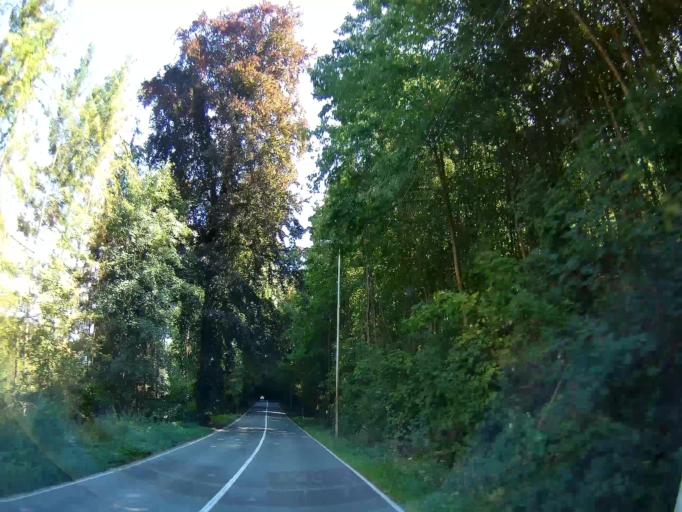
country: BE
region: Wallonia
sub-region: Province de Namur
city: Yvoir
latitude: 50.3386
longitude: 4.8612
